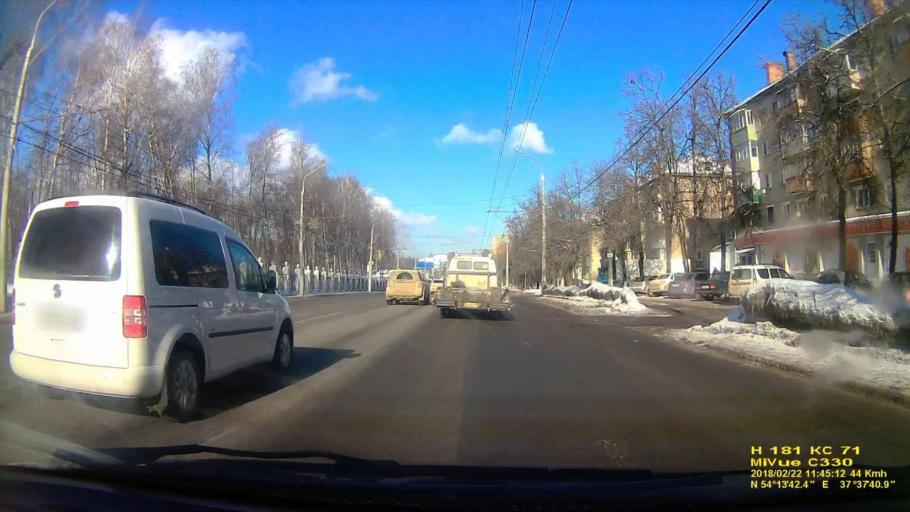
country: RU
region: Tula
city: Gorelki
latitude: 54.2286
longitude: 37.6280
